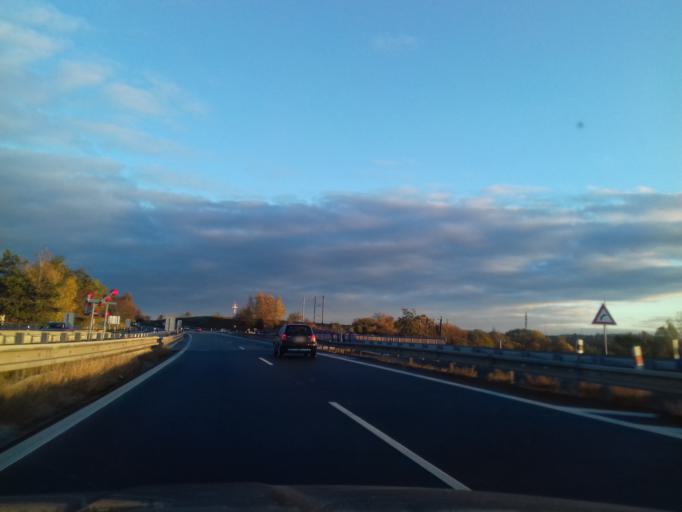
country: CZ
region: Olomoucky
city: Otaslavice
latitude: 49.3692
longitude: 17.0973
